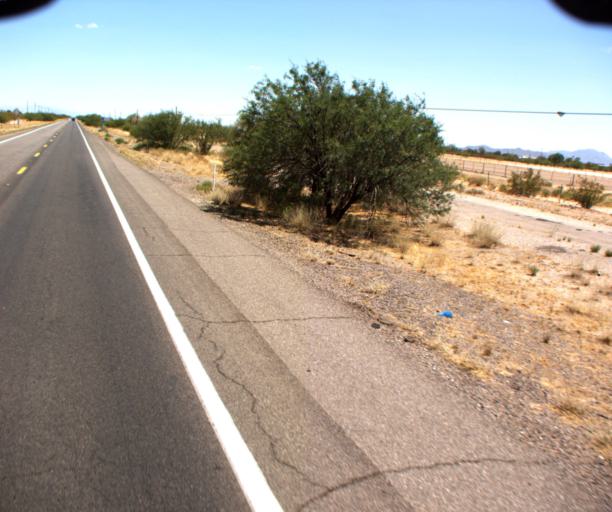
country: US
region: Arizona
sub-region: Pinal County
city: Florence
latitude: 32.9858
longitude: -111.3597
